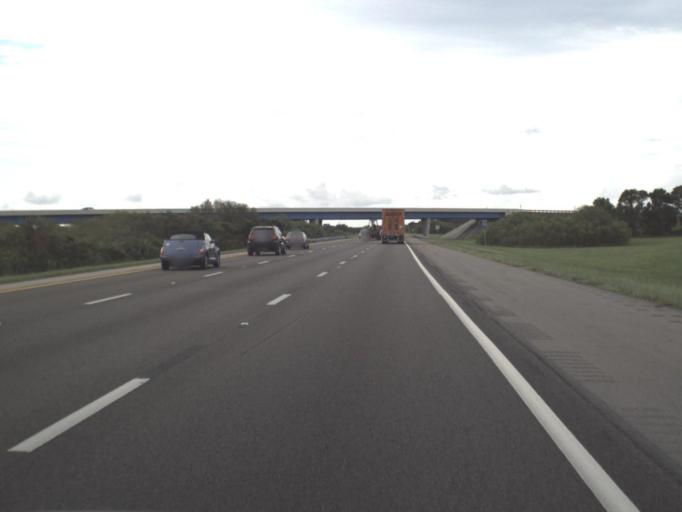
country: US
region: Florida
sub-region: Sarasota County
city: Osprey
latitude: 27.1926
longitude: -82.4395
